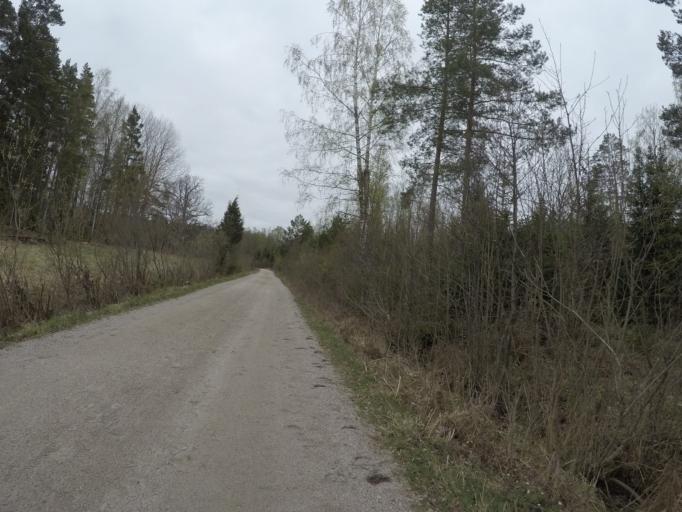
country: SE
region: Soedermanland
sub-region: Eskilstuna Kommun
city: Kvicksund
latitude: 59.3985
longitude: 16.2565
